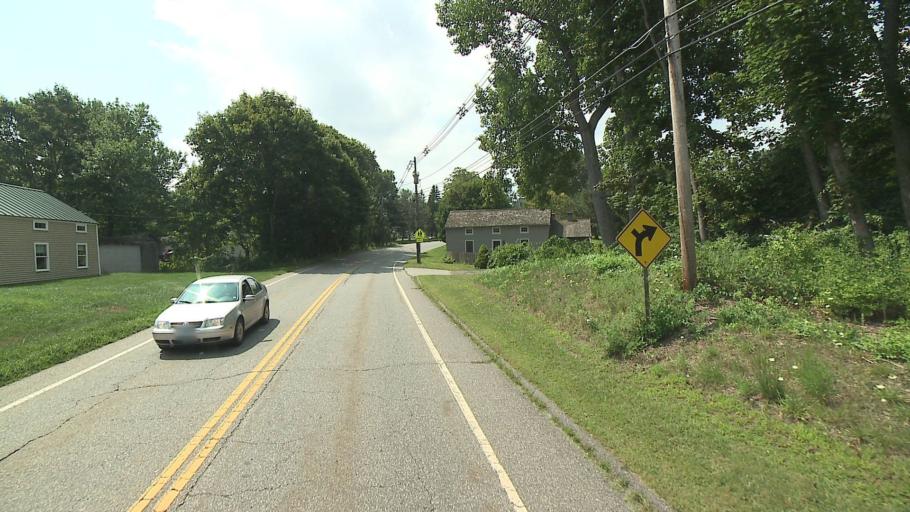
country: US
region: Connecticut
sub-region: Litchfield County
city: Bethlehem Village
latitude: 41.6852
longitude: -73.1960
